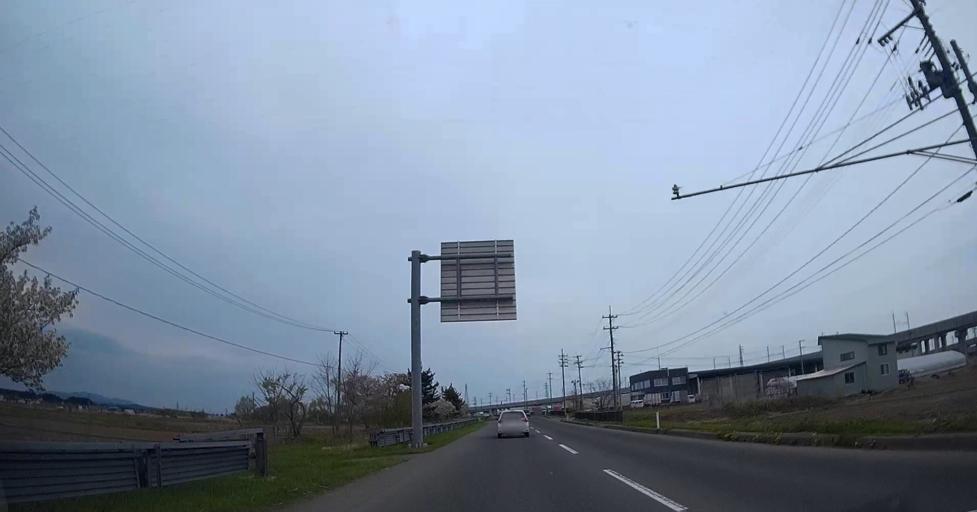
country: JP
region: Aomori
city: Aomori Shi
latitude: 40.8367
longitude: 140.6908
